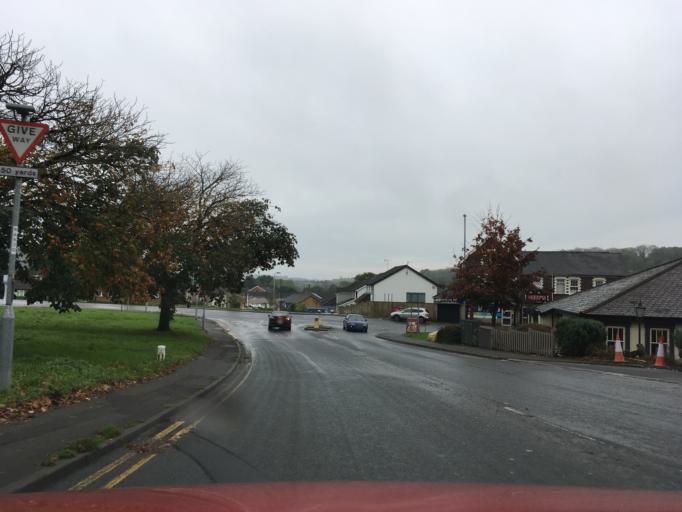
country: GB
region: Wales
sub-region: Newport
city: Caerleon
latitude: 51.5973
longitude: -2.9381
